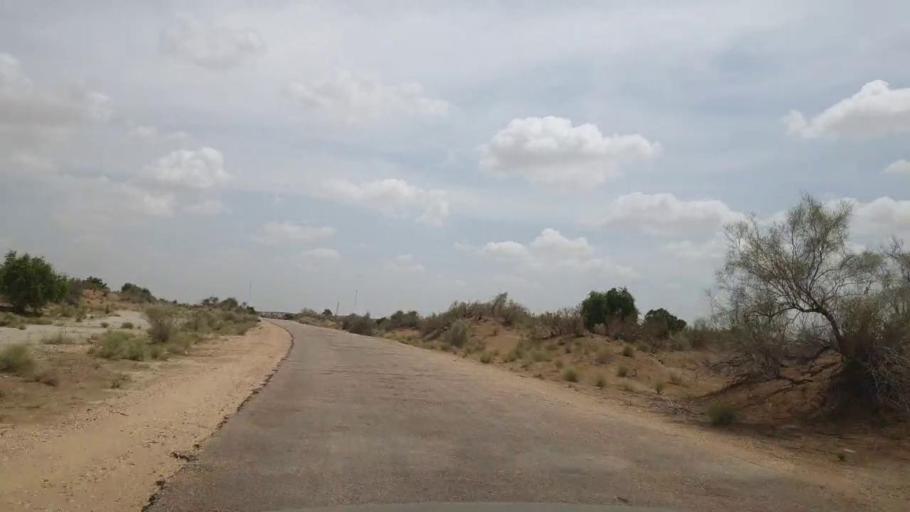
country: PK
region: Sindh
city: Kot Diji
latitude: 27.1432
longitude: 69.2245
